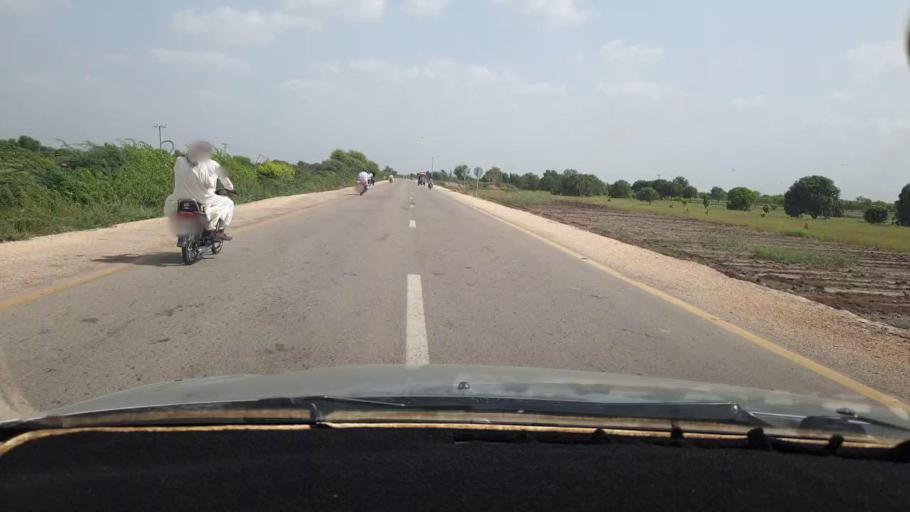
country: PK
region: Sindh
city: Digri
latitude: 25.0990
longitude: 69.1855
